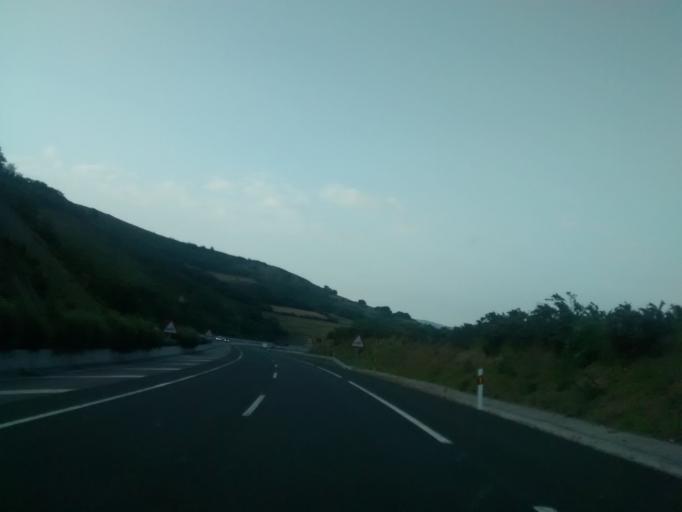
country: ES
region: Cantabria
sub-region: Provincia de Cantabria
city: Barcena de Pie de Concha
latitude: 43.1335
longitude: -4.0679
